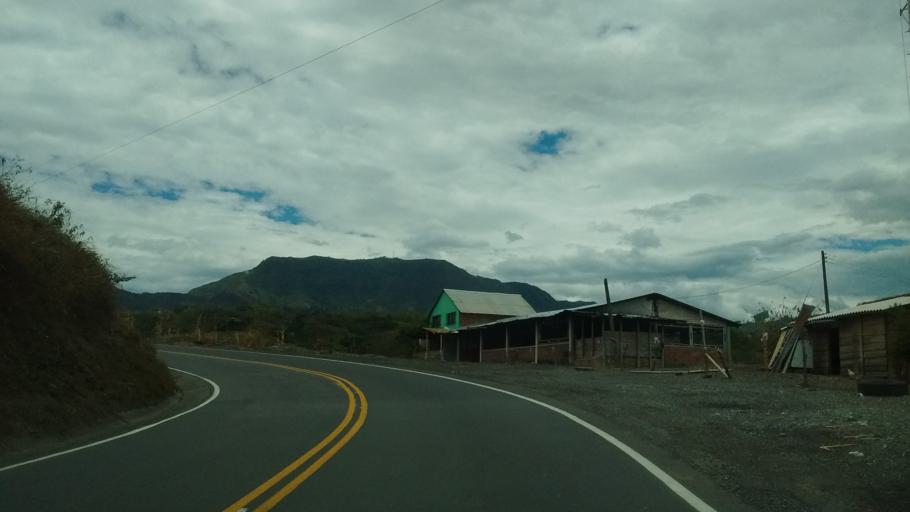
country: CO
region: Cauca
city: La Sierra
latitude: 2.2236
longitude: -76.7950
